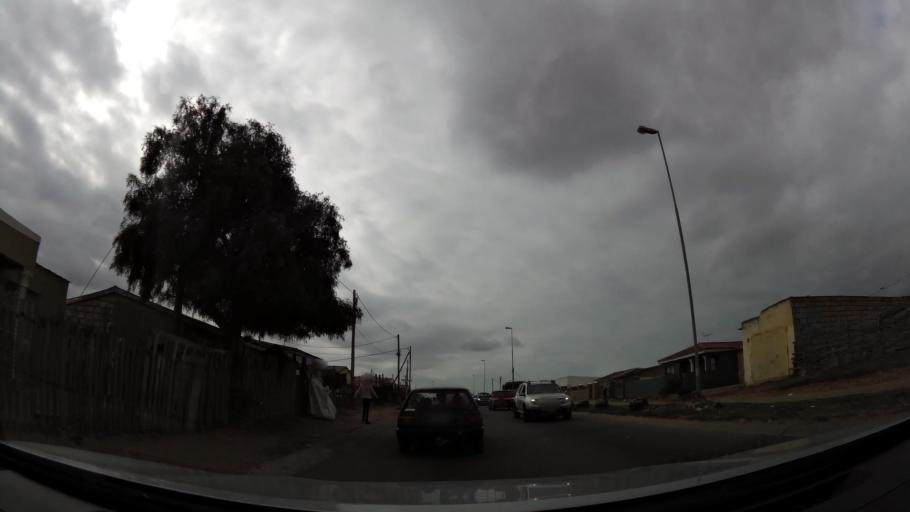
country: ZA
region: Eastern Cape
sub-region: Nelson Mandela Bay Metropolitan Municipality
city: Port Elizabeth
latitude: -33.8662
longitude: 25.5721
